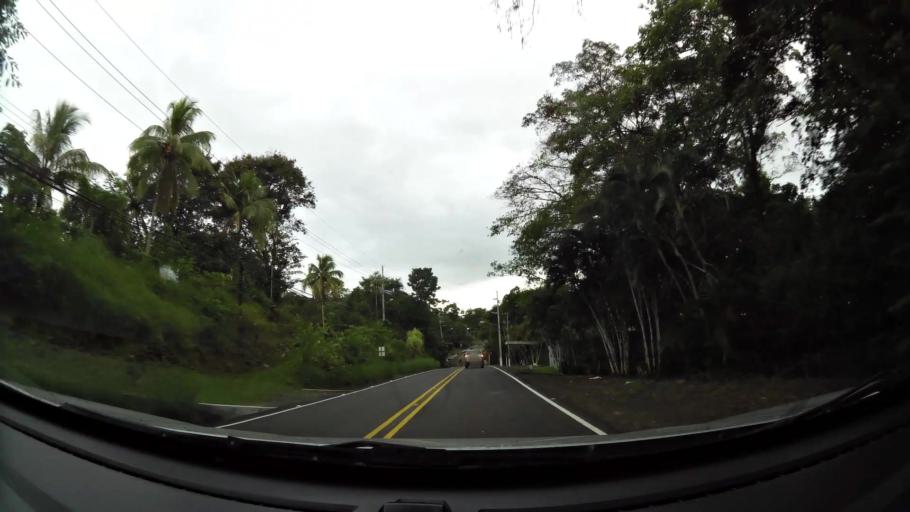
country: CR
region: Alajuela
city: Desamparados
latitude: 9.9417
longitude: -84.5393
